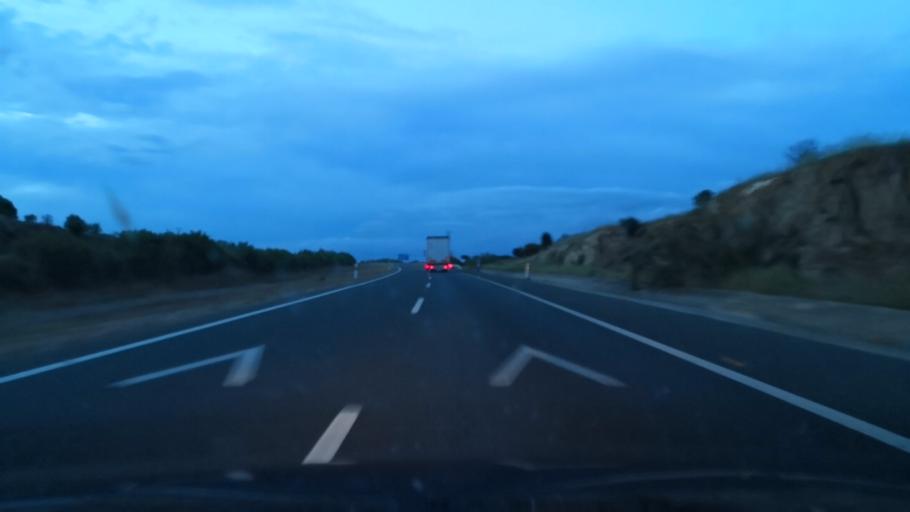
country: ES
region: Extremadura
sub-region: Provincia de Caceres
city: Santiago del Campo
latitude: 39.6360
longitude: -6.3931
